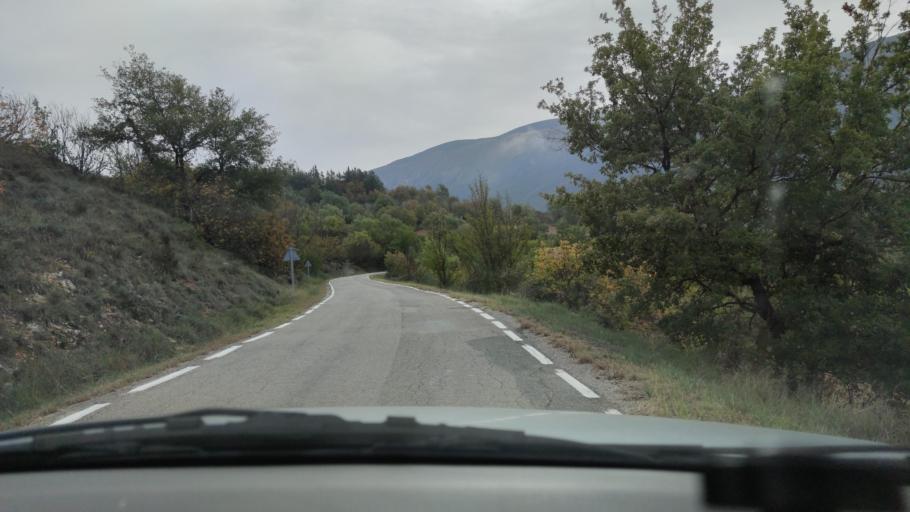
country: ES
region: Catalonia
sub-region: Provincia de Lleida
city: Llimiana
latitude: 42.0638
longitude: 0.9028
